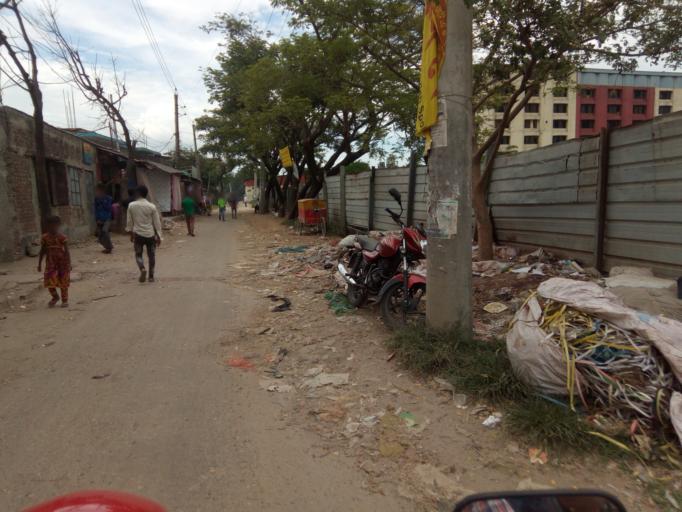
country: BD
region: Dhaka
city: Paltan
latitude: 23.7192
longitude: 90.4820
